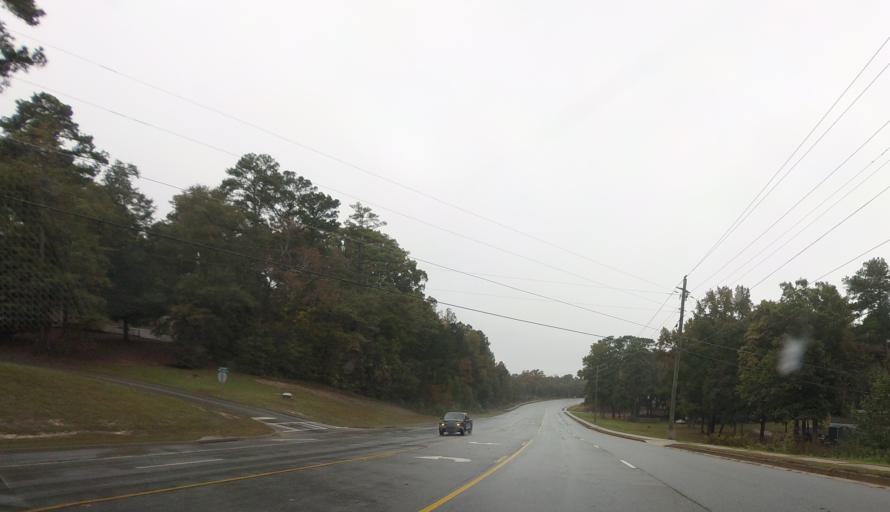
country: US
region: Georgia
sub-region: Houston County
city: Centerville
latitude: 32.6093
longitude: -83.6661
